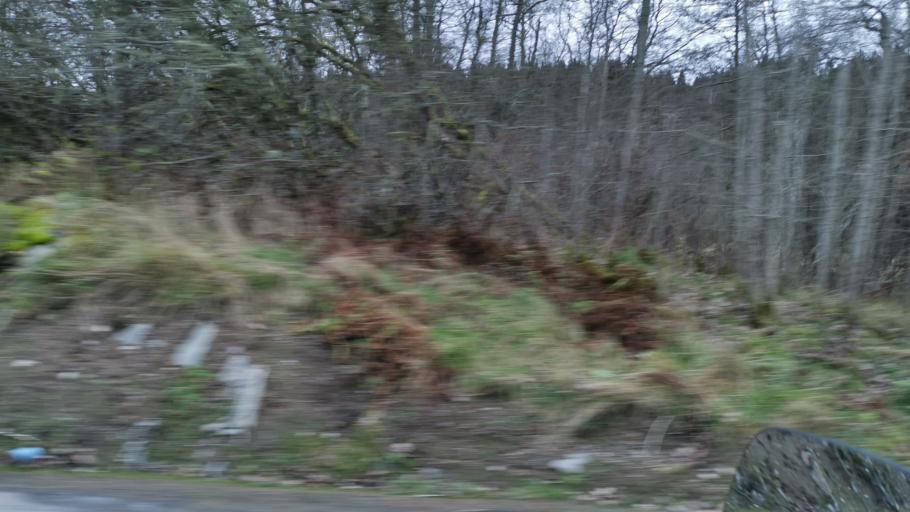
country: SE
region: Vaestra Goetaland
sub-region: Orust
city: Henan
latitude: 58.2505
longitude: 11.7210
